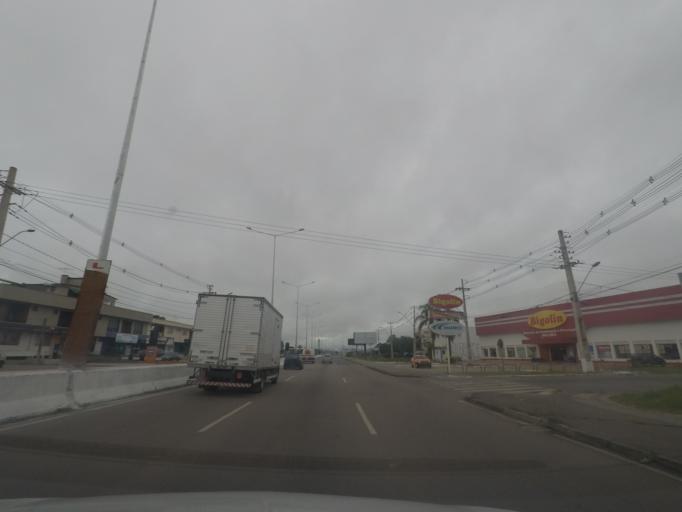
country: BR
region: Parana
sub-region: Pinhais
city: Pinhais
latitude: -25.4350
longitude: -49.1718
